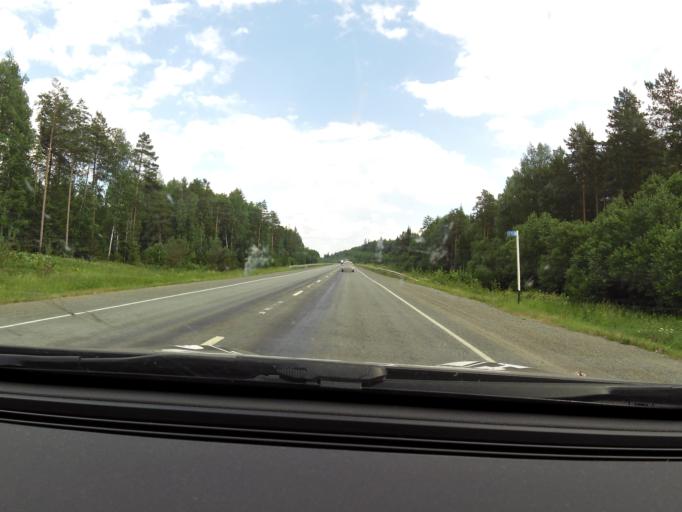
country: RU
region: Sverdlovsk
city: Bisert'
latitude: 56.8273
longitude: 58.9853
